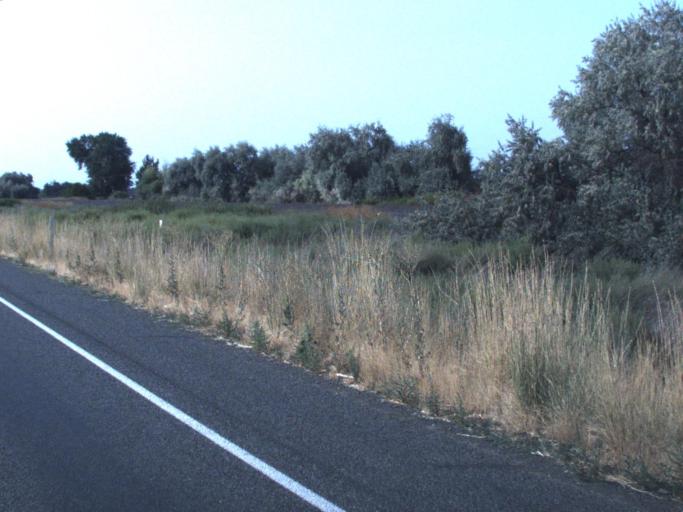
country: US
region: Washington
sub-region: Yakima County
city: Granger
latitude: 46.2860
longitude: -120.1735
